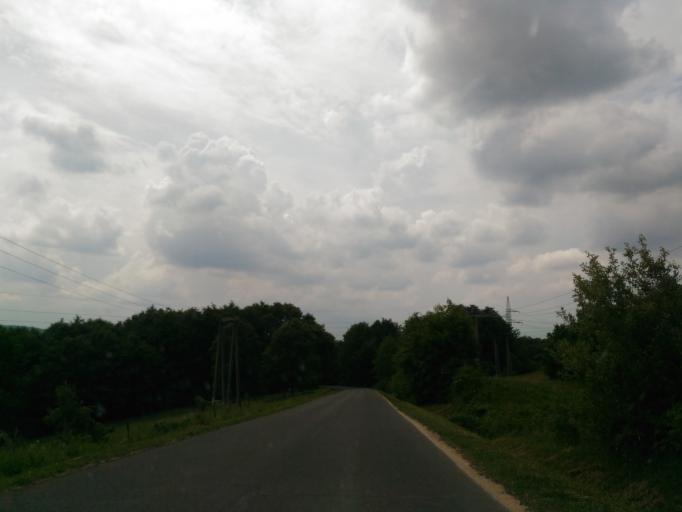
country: HU
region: Baranya
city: Komlo
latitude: 46.1828
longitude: 18.2360
